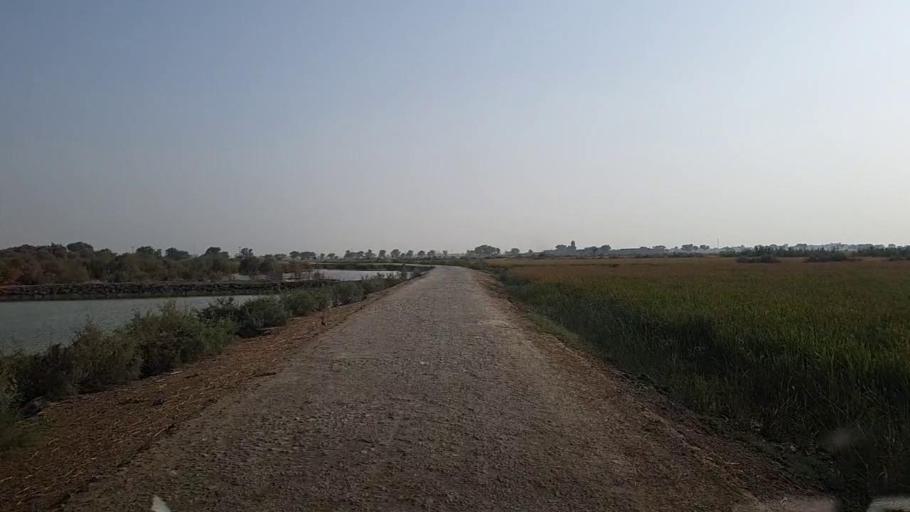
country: PK
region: Sindh
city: Kandhkot
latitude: 28.2897
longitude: 69.2566
